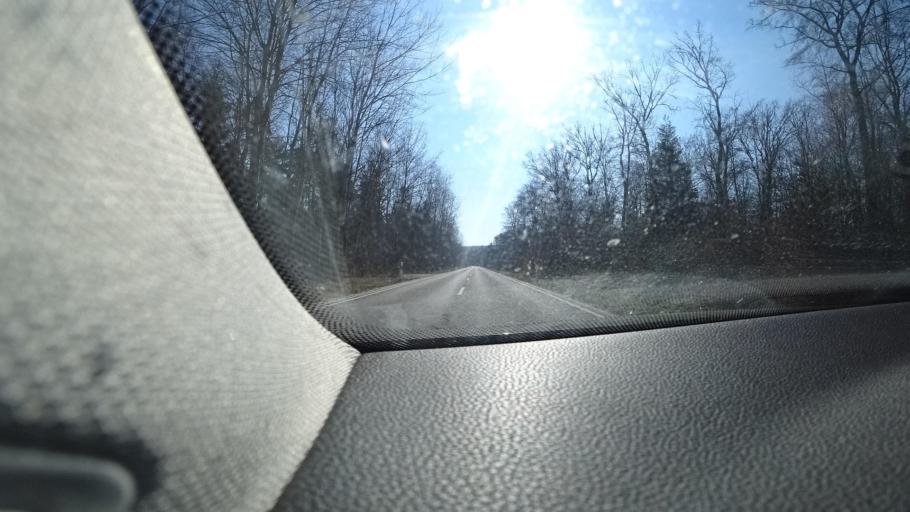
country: DE
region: Rheinland-Pfalz
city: Argenthal
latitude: 49.9672
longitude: 7.6036
